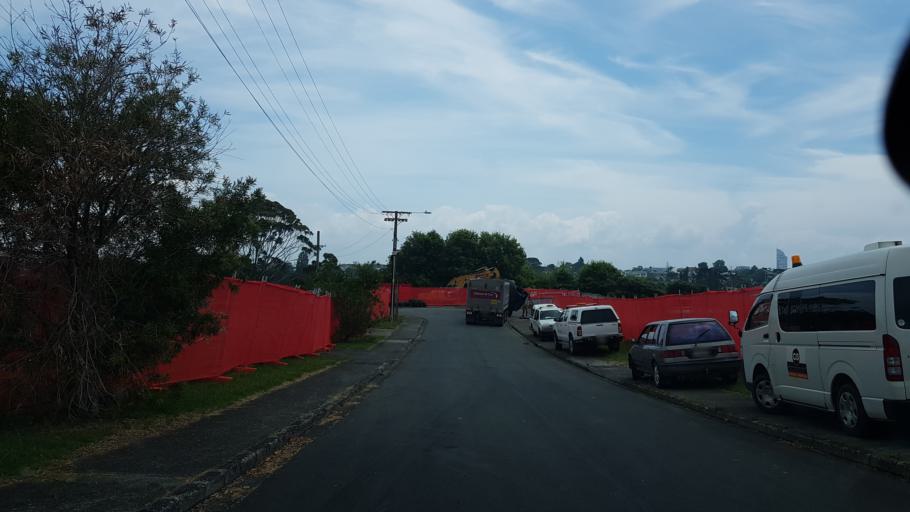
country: NZ
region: Auckland
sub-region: Auckland
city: North Shore
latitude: -36.8049
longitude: 174.7827
